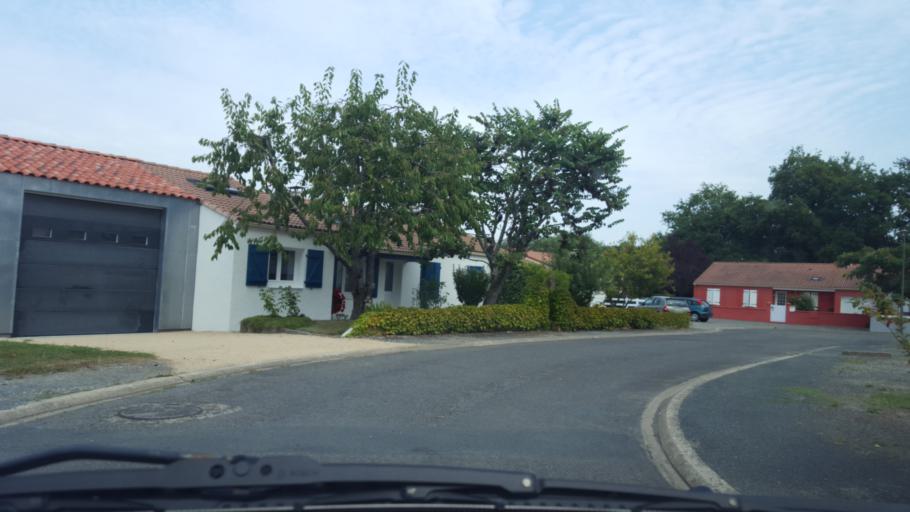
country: FR
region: Pays de la Loire
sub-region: Departement de la Loire-Atlantique
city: Saint-Philbert-de-Grand-Lieu
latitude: 47.0335
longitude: -1.6334
